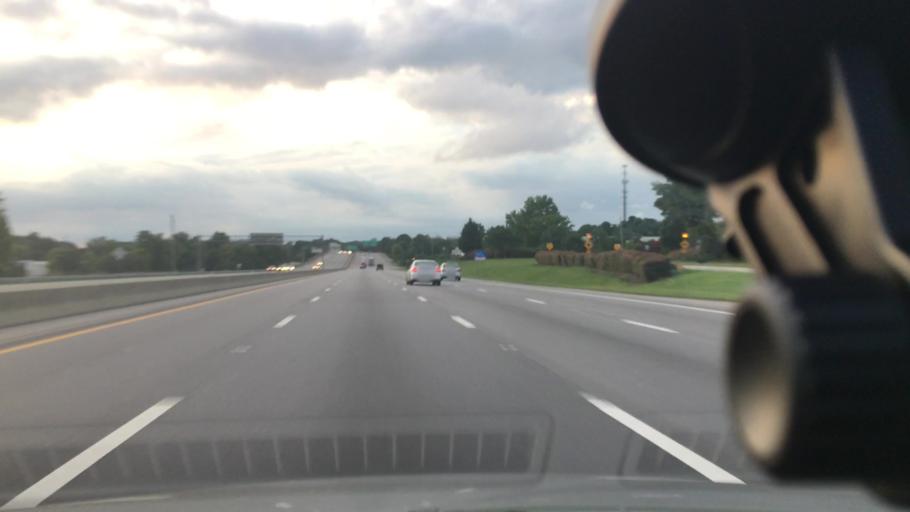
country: US
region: North Carolina
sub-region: Wake County
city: Raleigh
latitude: 35.8038
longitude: -78.5949
